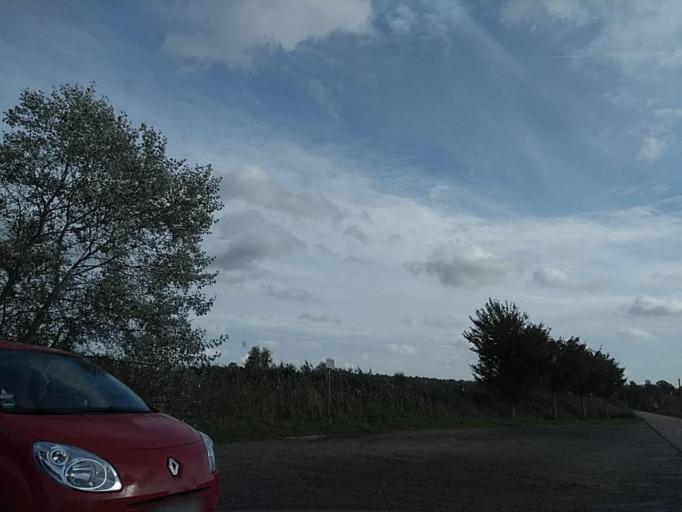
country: DE
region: Mecklenburg-Vorpommern
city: Seeheilbad Graal-Muritz
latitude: 54.2616
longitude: 12.2521
